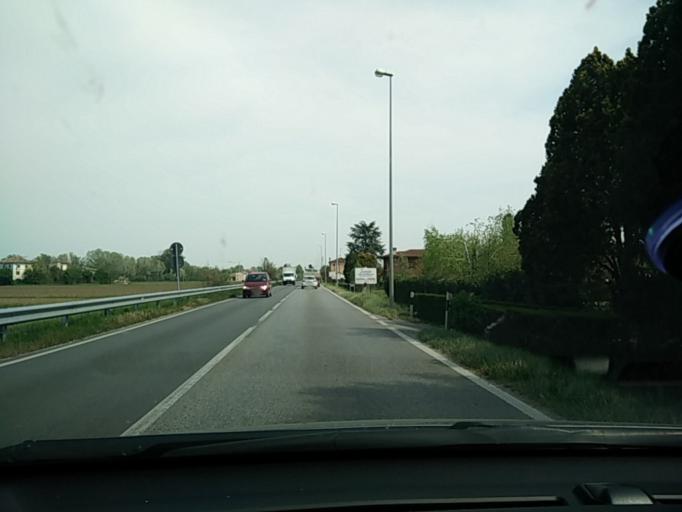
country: IT
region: Veneto
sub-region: Provincia di Treviso
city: Cosniga-Zoppe
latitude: 45.8701
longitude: 12.3763
